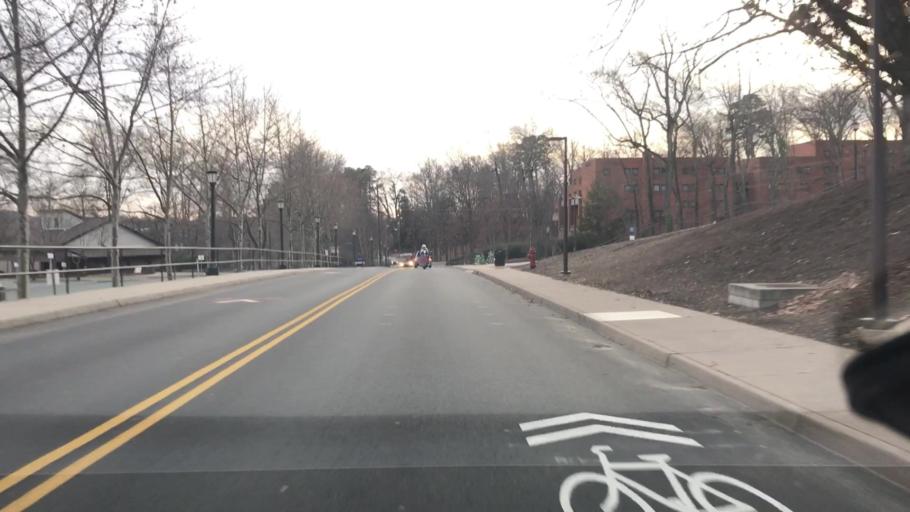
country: US
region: Virginia
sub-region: City of Charlottesville
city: Charlottesville
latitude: 38.0310
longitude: -78.5155
